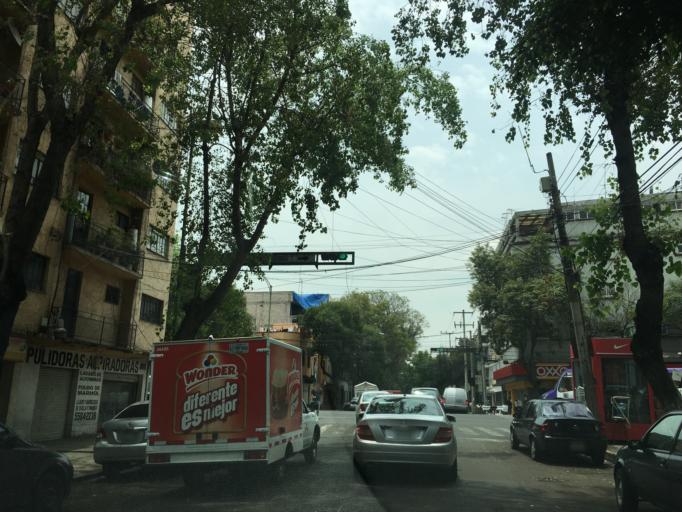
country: MX
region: Mexico City
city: Benito Juarez
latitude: 19.4067
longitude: -99.1598
